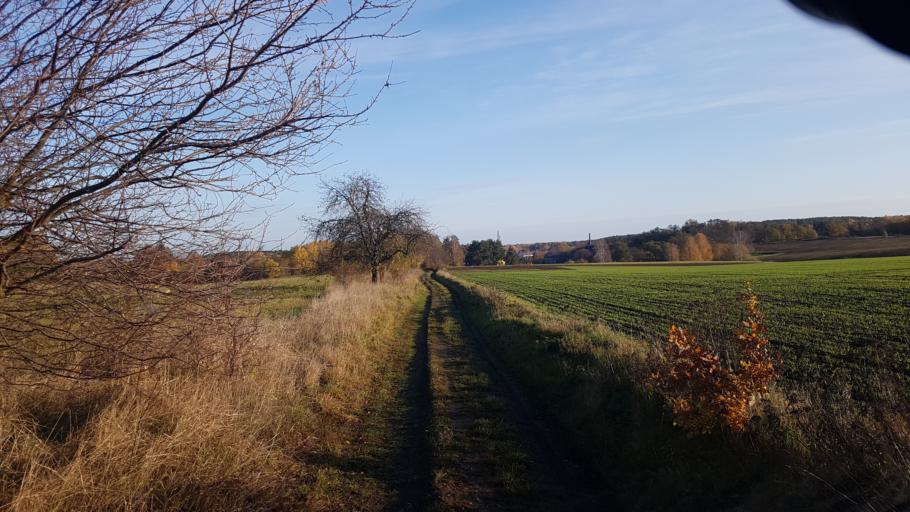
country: DE
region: Brandenburg
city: Crinitz
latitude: 51.7328
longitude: 13.7529
